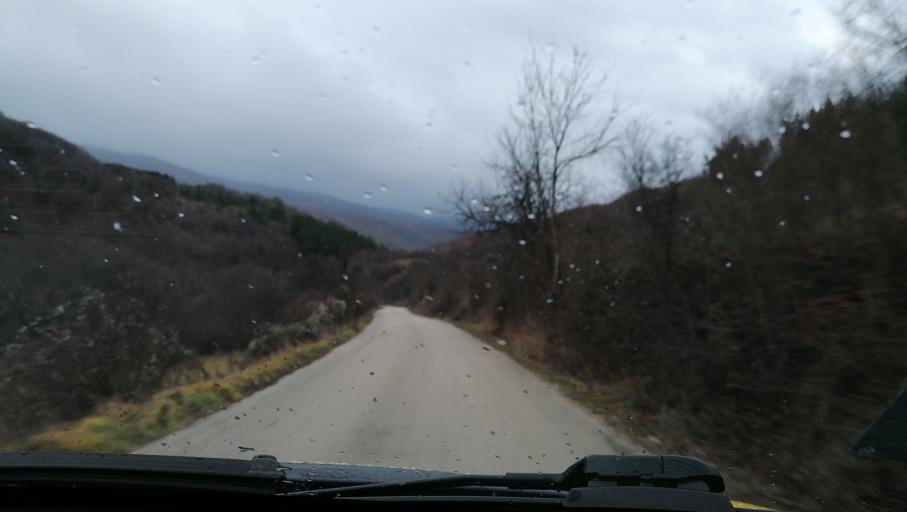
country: RS
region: Central Serbia
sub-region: Pirotski Okrug
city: Dimitrovgrad
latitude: 42.9771
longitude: 22.6548
